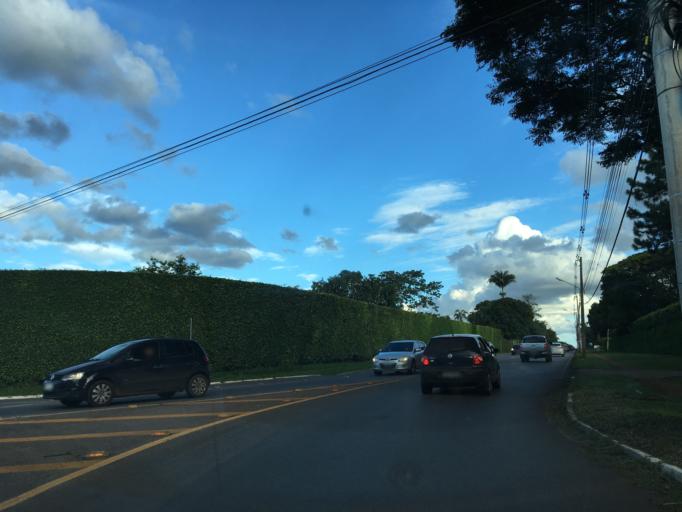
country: BR
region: Federal District
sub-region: Brasilia
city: Brasilia
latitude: -15.8468
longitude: -47.8873
